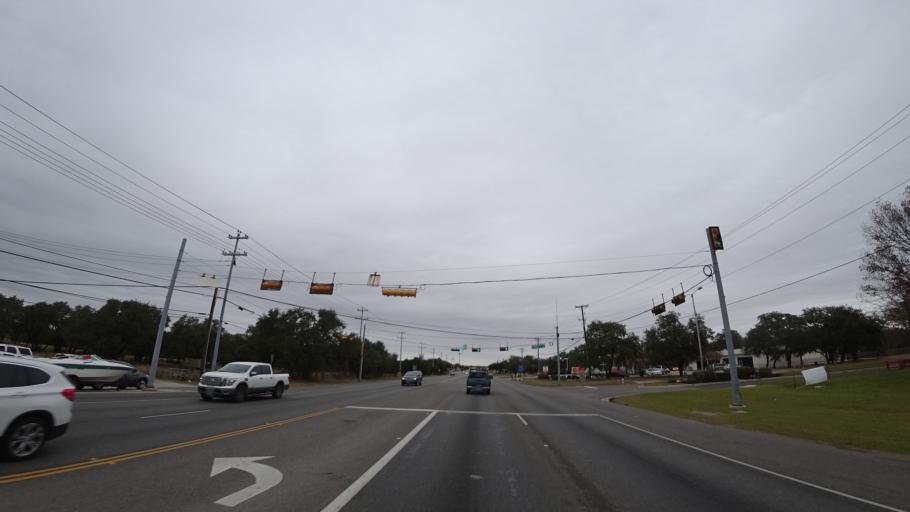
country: US
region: Texas
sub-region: Williamson County
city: Anderson Mill
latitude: 30.4431
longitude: -97.8332
